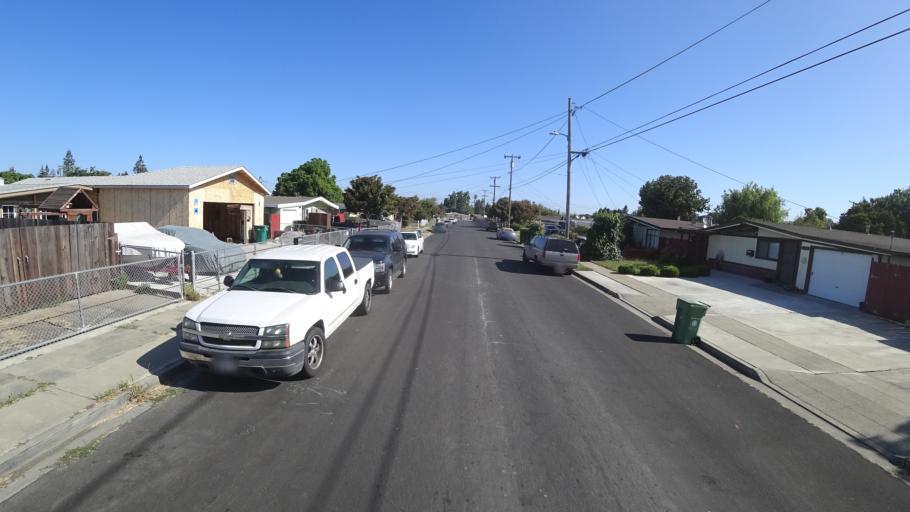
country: US
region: California
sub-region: Alameda County
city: Hayward
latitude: 37.6293
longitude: -122.0809
